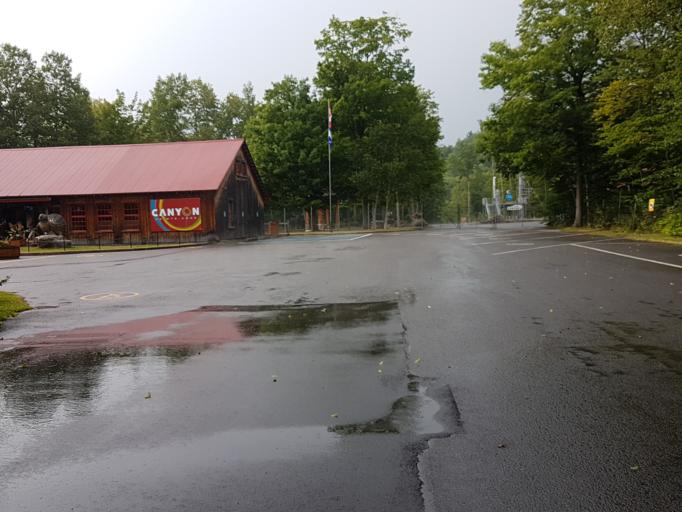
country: CA
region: Quebec
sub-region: Capitale-Nationale
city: Beaupre
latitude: 47.0722
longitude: -70.8744
